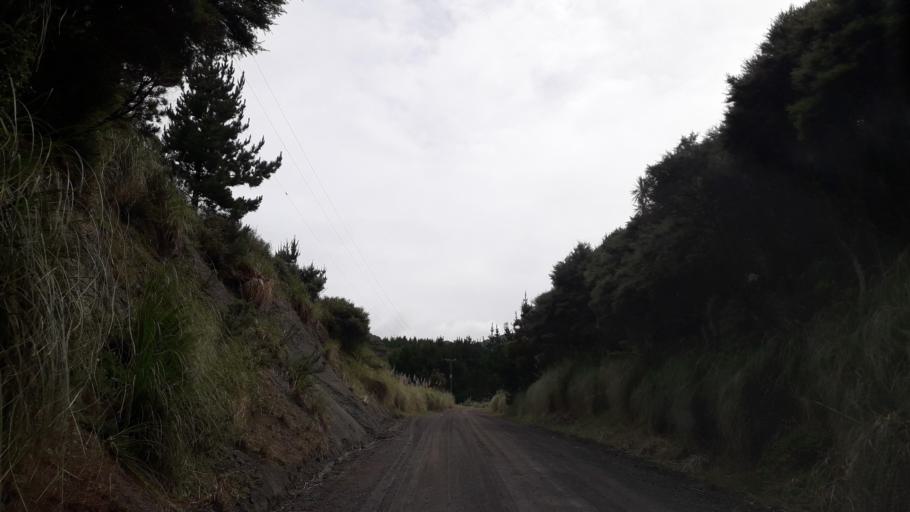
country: NZ
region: Northland
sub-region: Far North District
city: Ahipara
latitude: -35.4357
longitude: 173.3318
